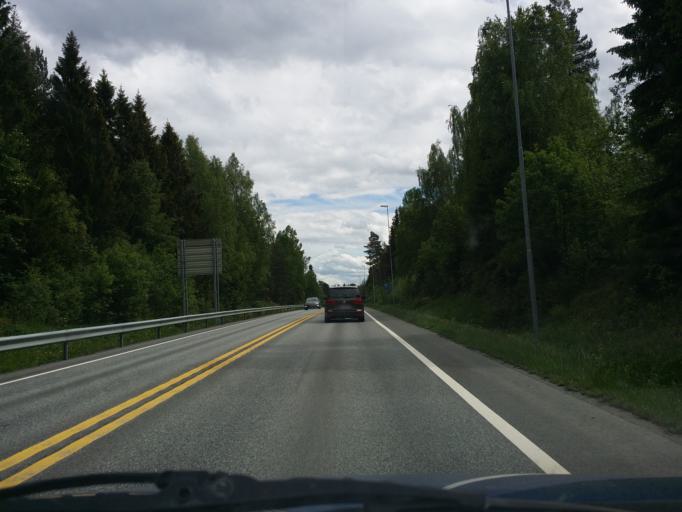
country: NO
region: Hedmark
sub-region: Stange
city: Stange
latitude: 60.7192
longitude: 11.2395
